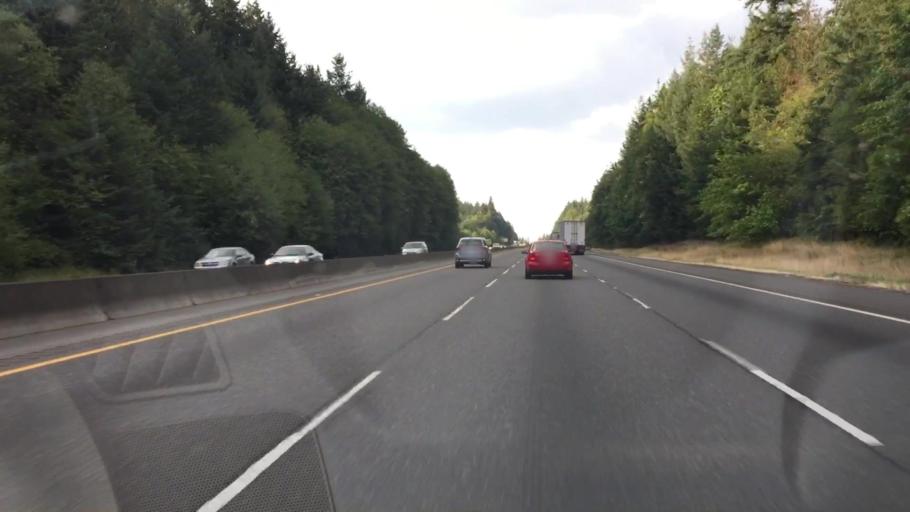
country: US
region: Washington
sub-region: Cowlitz County
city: Castle Rock
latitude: 46.3384
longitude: -122.9076
